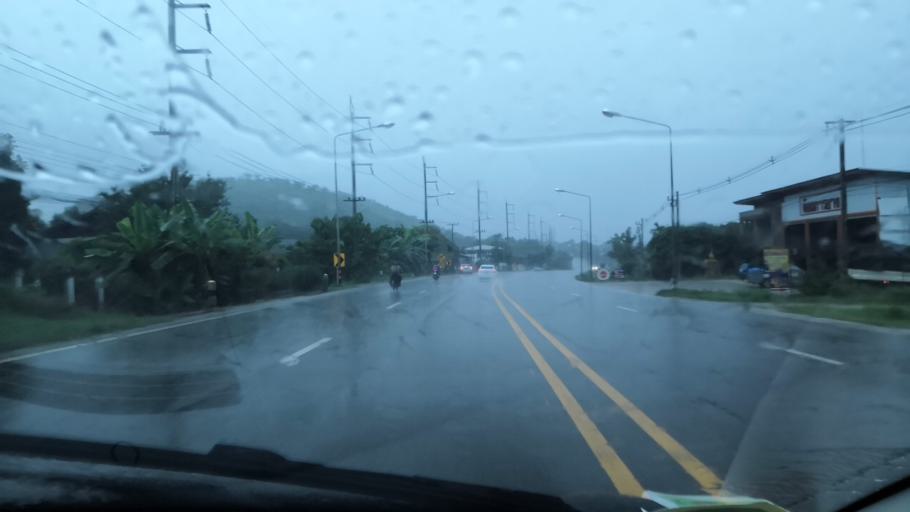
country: TH
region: Chiang Mai
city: Chom Thong
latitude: 18.3582
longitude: 98.6793
